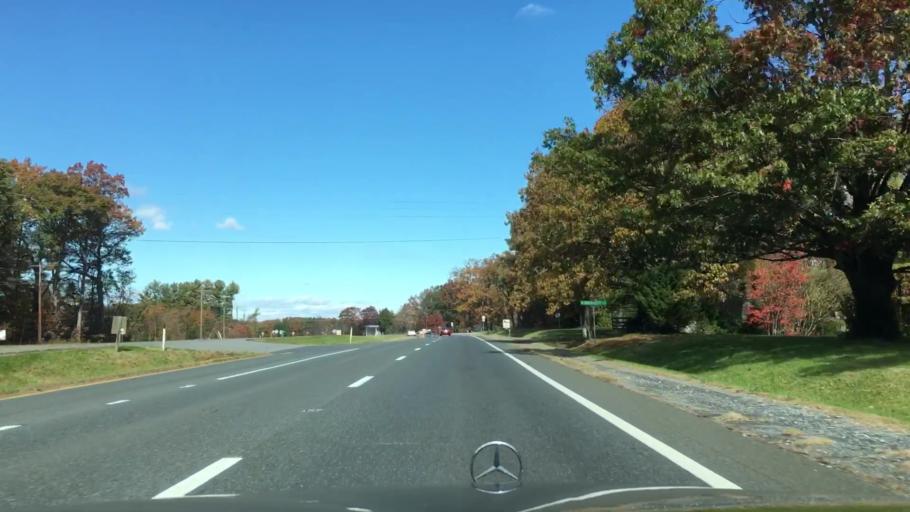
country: US
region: Virginia
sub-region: Campbell County
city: Rustburg
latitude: 37.2339
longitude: -79.1856
